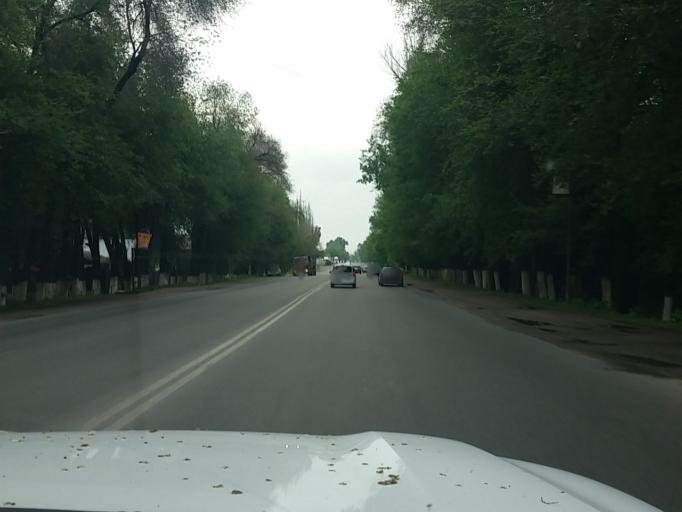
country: KZ
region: Almaty Oblysy
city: Energeticheskiy
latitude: 43.3407
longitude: 77.0456
